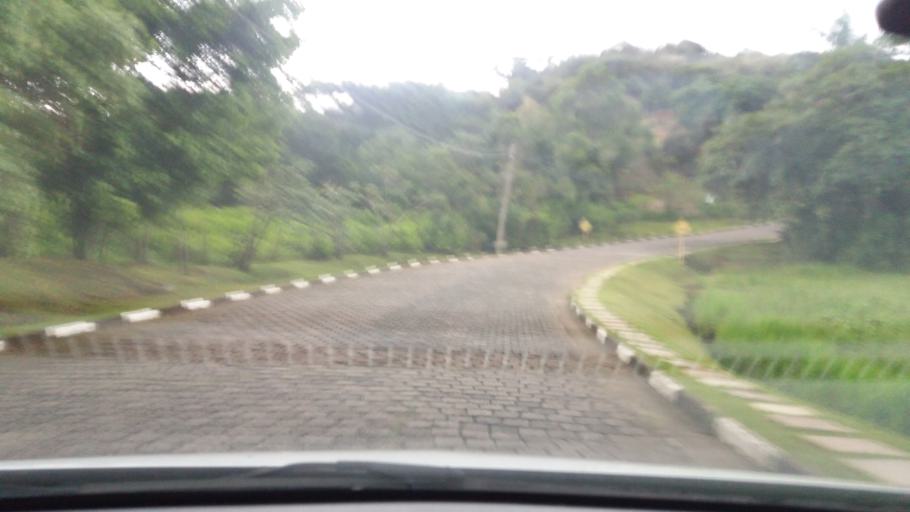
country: BR
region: Sao Paulo
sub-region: Bom Jesus Dos Perdoes
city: Bom Jesus dos Perdoes
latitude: -23.1631
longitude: -46.4531
